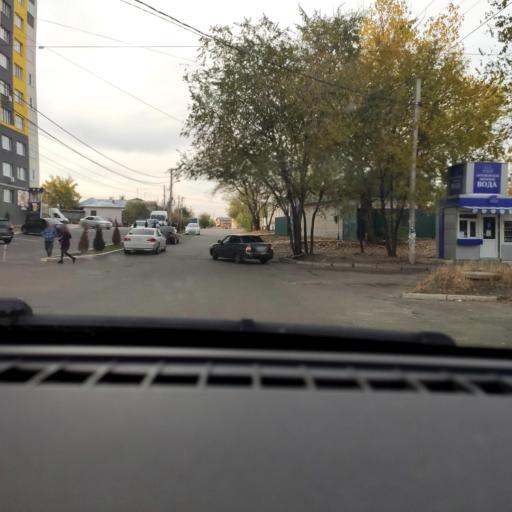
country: RU
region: Voronezj
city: Voronezh
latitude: 51.7049
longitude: 39.2732
